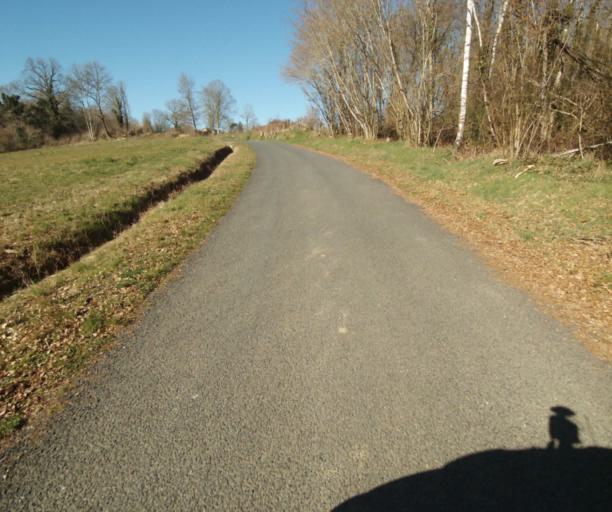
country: FR
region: Limousin
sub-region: Departement de la Correze
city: Chamboulive
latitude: 45.4194
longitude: 1.6475
